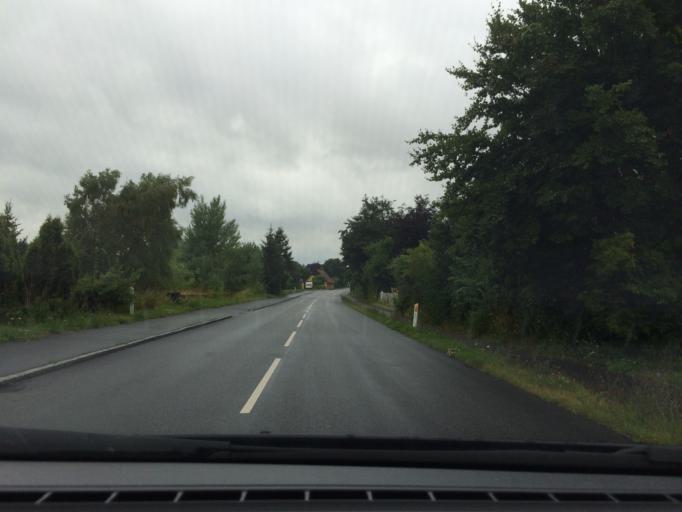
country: DK
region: Zealand
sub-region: Vordingborg Kommune
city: Stege
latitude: 54.9956
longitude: 12.3954
